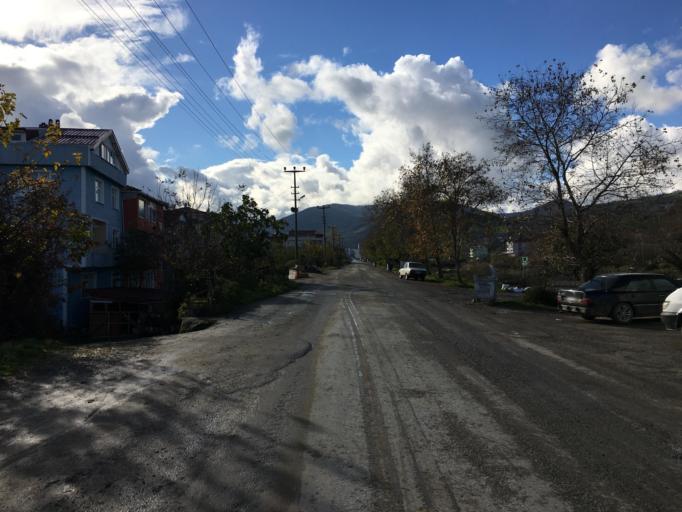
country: TR
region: Samsun
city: Alacam
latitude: 41.6149
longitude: 35.6008
